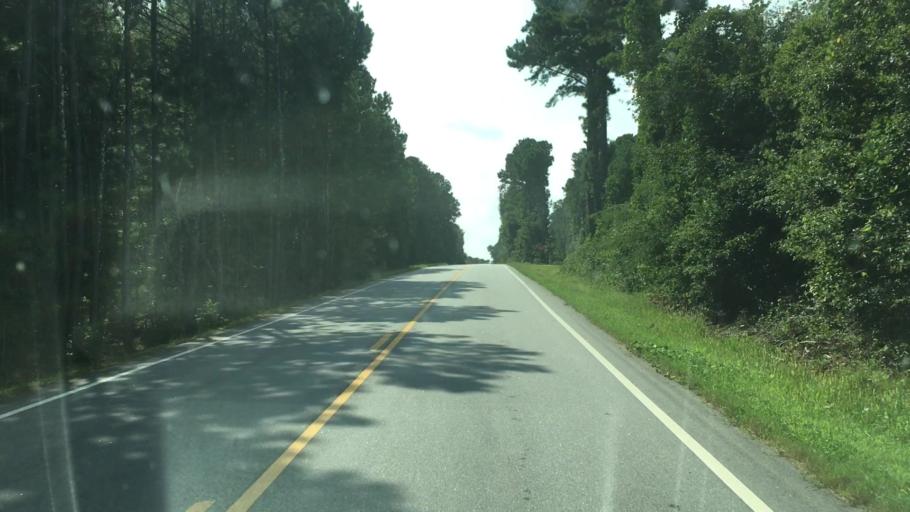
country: US
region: Georgia
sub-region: Jasper County
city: Monticello
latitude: 33.3552
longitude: -83.7410
